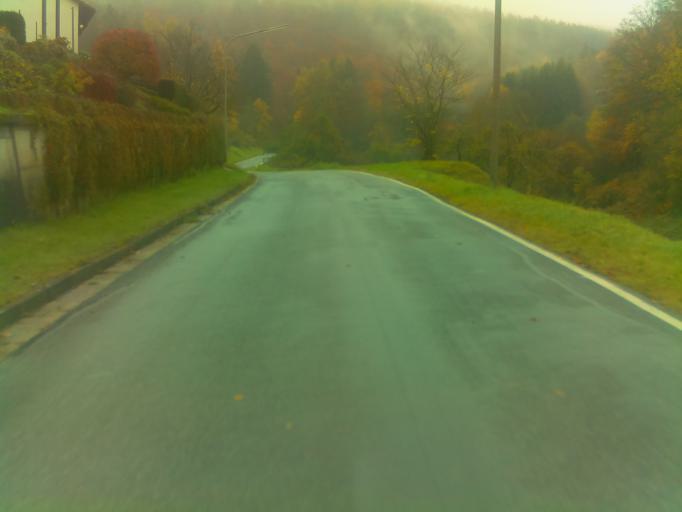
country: DE
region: Hesse
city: Neckarsteinach
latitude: 49.4381
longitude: 8.8460
